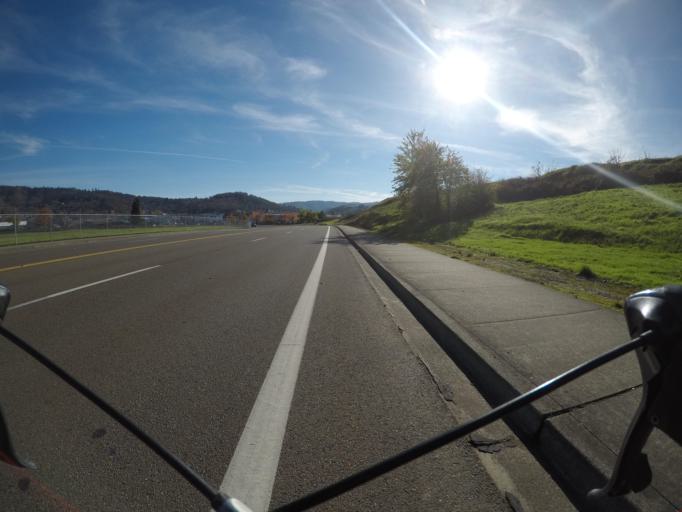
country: US
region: Oregon
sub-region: Douglas County
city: Roseburg
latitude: 43.2316
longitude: -123.3568
